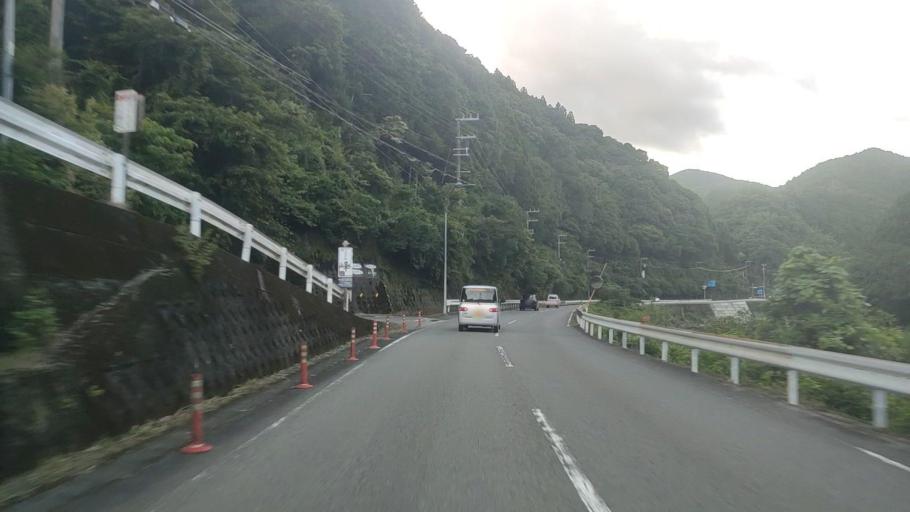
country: JP
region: Wakayama
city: Tanabe
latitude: 33.7852
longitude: 135.5051
